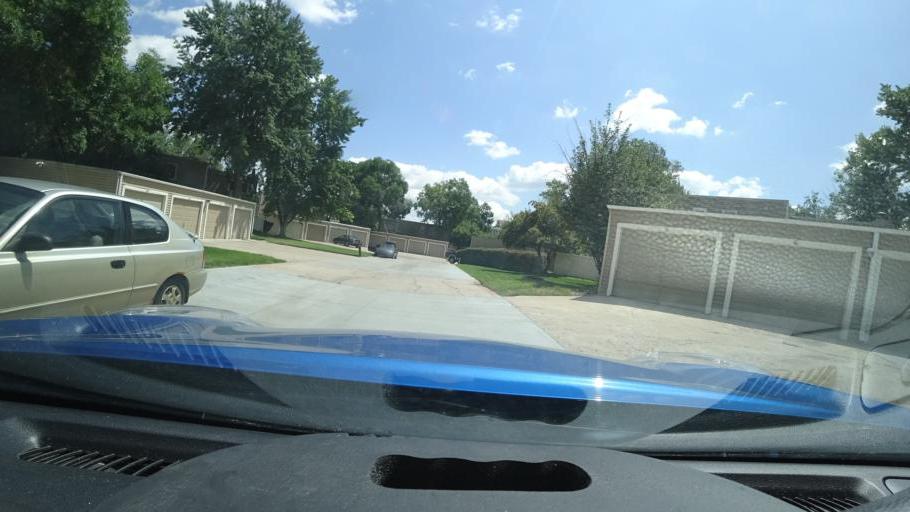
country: US
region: Colorado
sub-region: Adams County
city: Aurora
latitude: 39.6955
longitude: -104.8767
